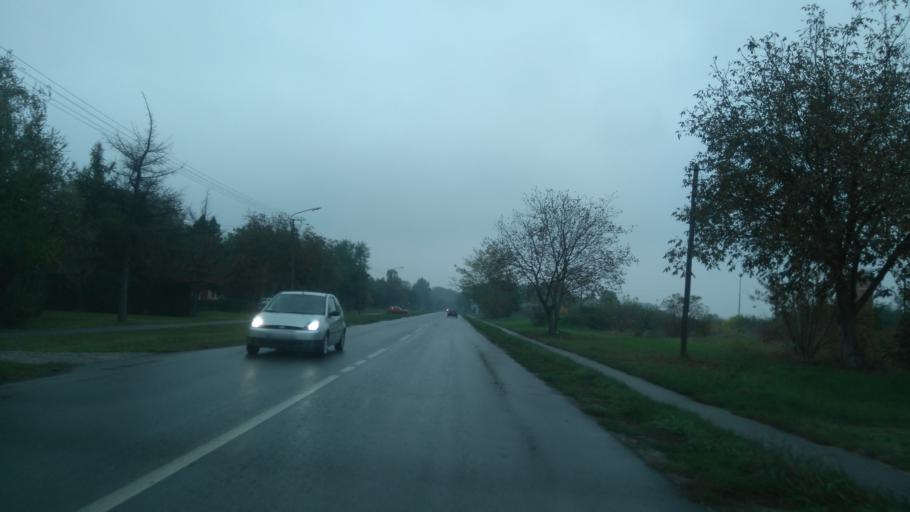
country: RS
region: Autonomna Pokrajina Vojvodina
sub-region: Juznobacki Okrug
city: Becej
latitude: 45.6271
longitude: 20.0353
